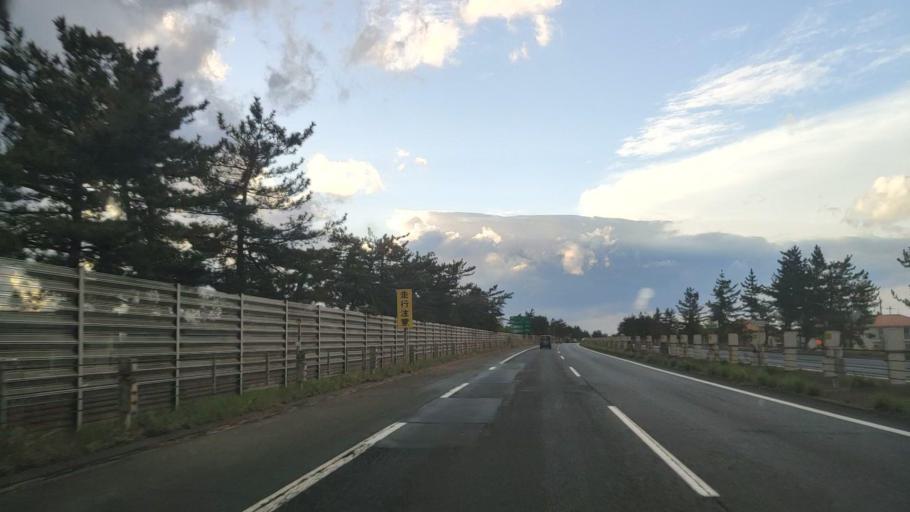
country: JP
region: Iwate
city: Mizusawa
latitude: 39.1914
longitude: 141.1115
